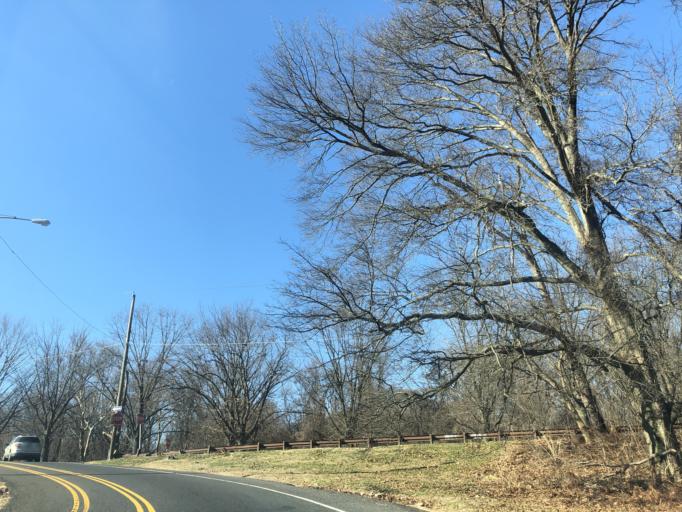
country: US
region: Pennsylvania
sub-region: Montgomery County
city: Bala-Cynwyd
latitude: 40.0003
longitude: -75.1992
